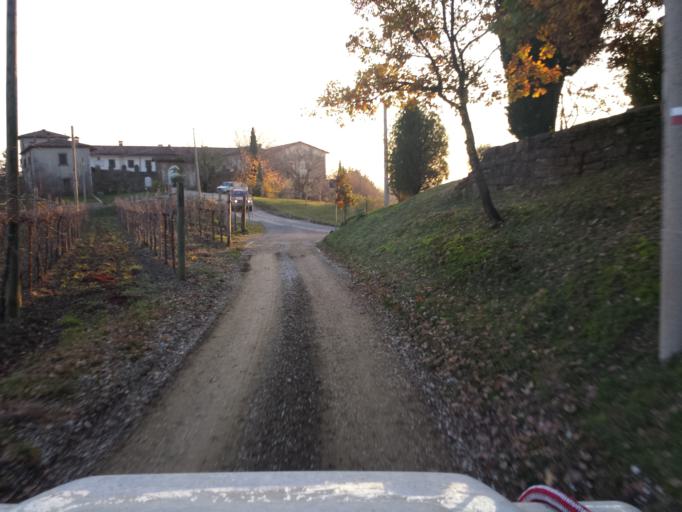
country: IT
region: Friuli Venezia Giulia
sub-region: Provincia di Gorizia
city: Dolegna del Collio
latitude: 46.0167
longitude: 13.4820
